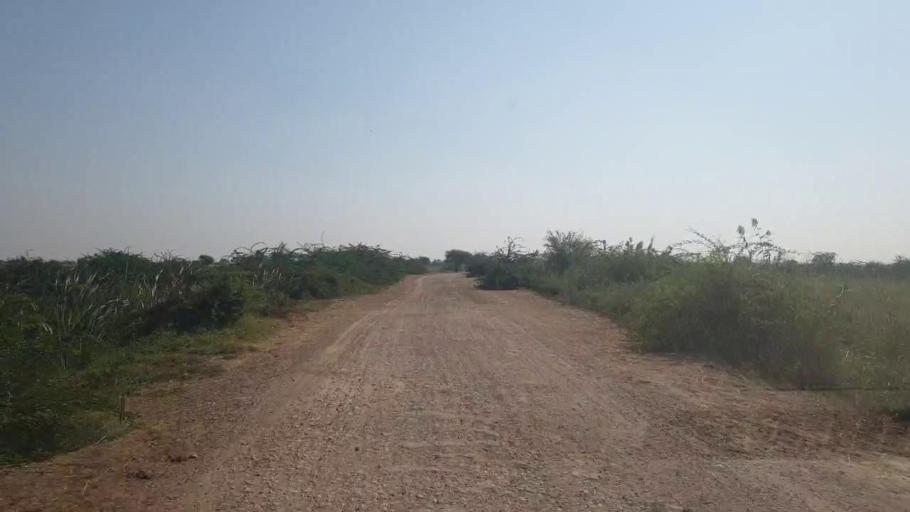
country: PK
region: Sindh
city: Badin
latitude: 24.5619
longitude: 68.8459
